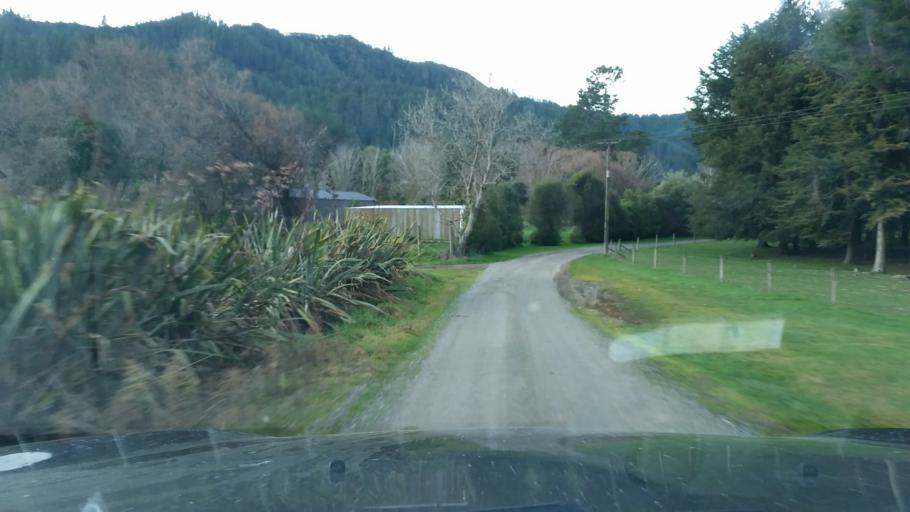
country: NZ
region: Marlborough
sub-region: Marlborough District
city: Blenheim
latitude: -41.4742
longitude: 173.7412
